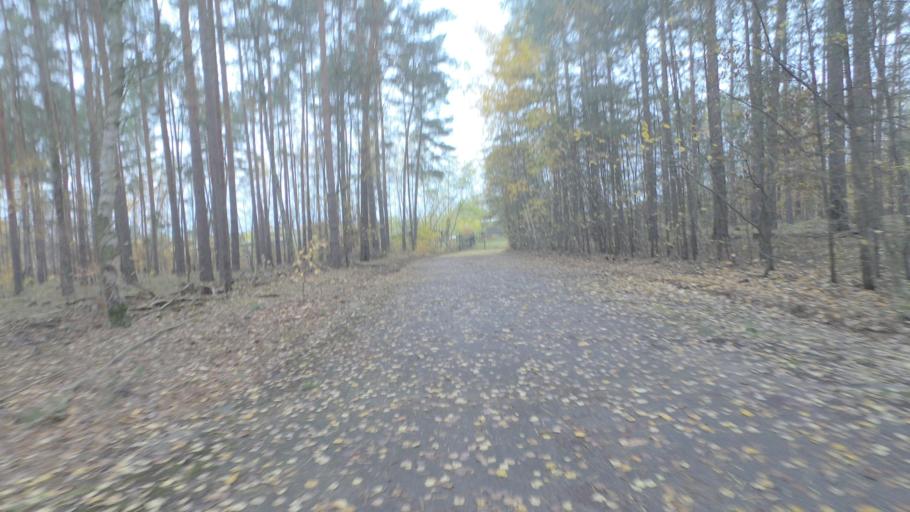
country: DE
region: Brandenburg
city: Rangsdorf
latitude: 52.3196
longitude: 13.4062
